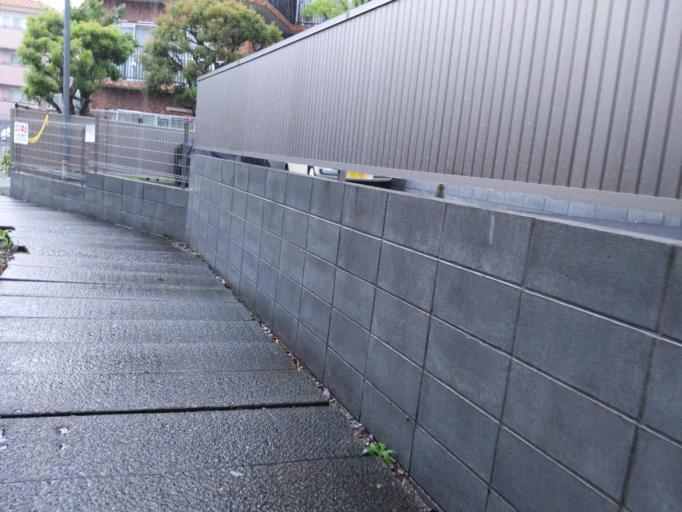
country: JP
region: Tokyo
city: Chofugaoka
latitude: 35.6044
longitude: 139.6240
